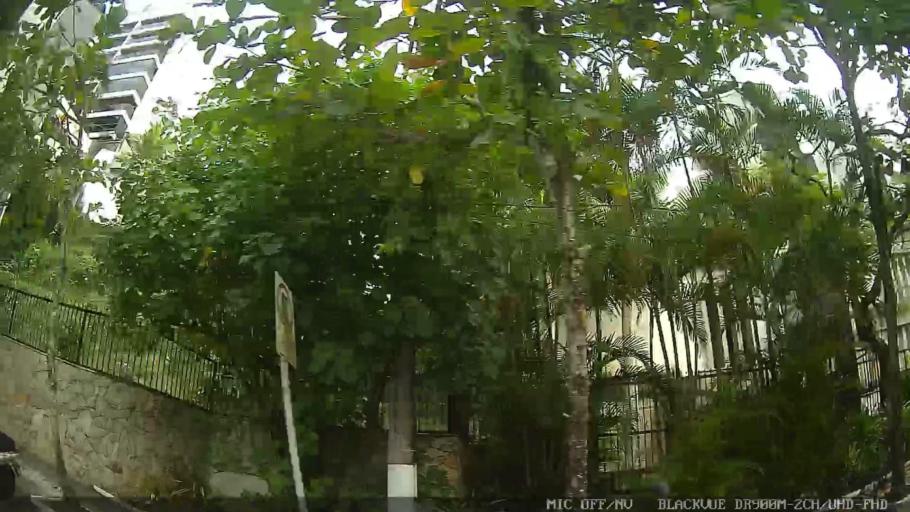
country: BR
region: Sao Paulo
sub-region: Guaruja
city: Guaruja
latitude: -23.9940
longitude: -46.1996
